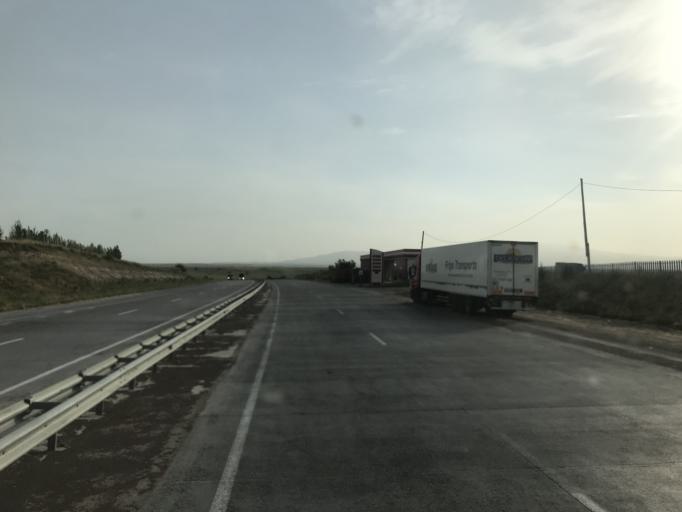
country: UZ
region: Toshkent
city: Qibray
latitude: 41.5278
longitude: 69.4013
